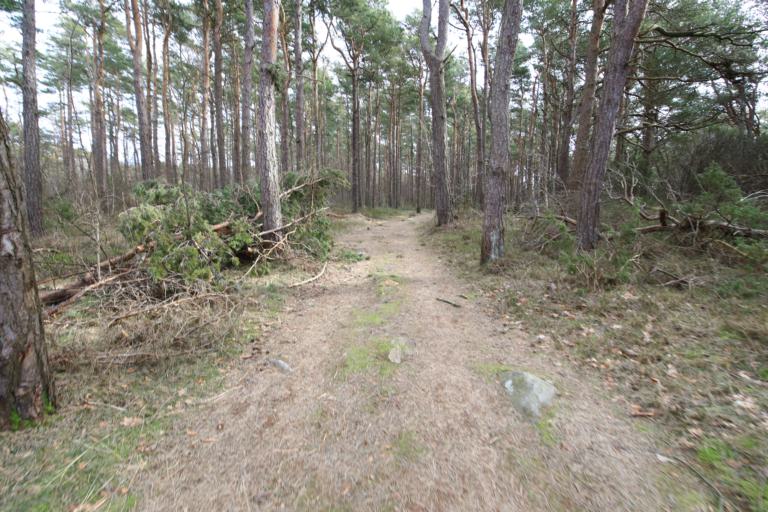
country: SE
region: Halland
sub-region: Kungsbacka Kommun
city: Frillesas
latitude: 57.2325
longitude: 12.1039
